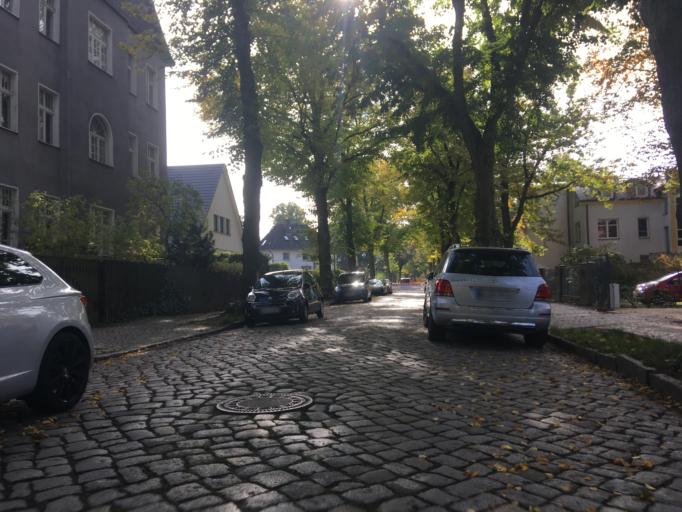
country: DE
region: Berlin
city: Lichtenrade
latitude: 52.3852
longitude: 13.4032
